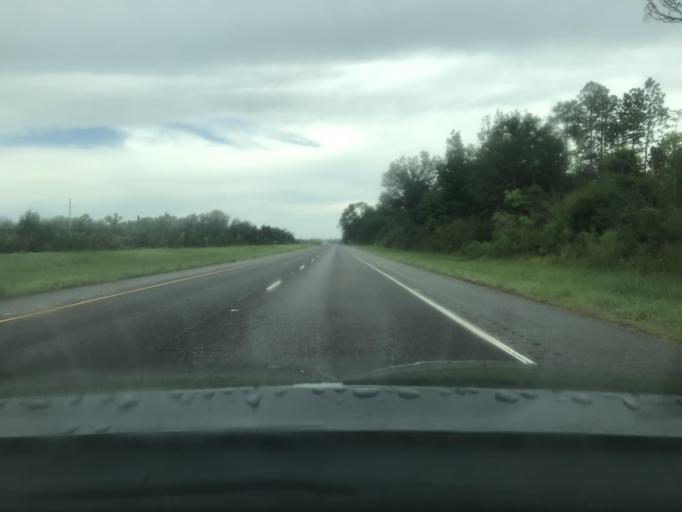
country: US
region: Louisiana
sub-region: Calcasieu Parish
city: Moss Bluff
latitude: 30.3874
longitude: -93.2181
